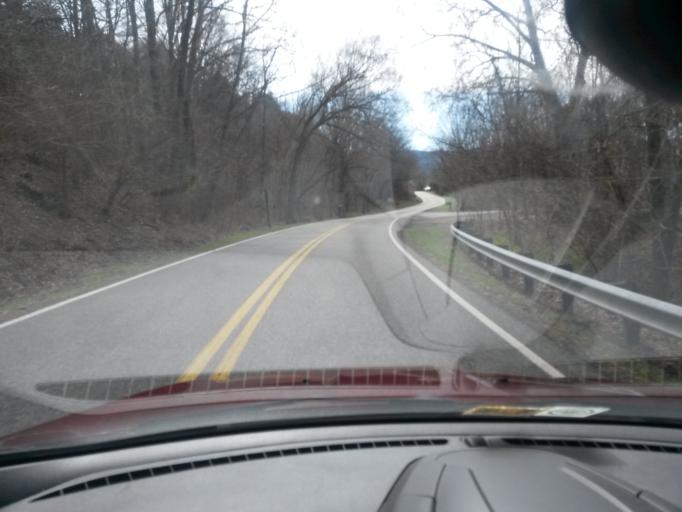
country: US
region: West Virginia
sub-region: Greenbrier County
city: White Sulphur Springs
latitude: 37.6424
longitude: -80.2381
